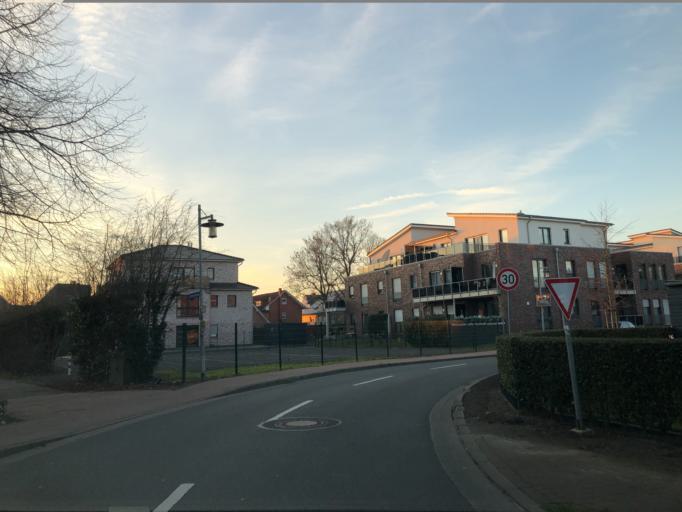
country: DE
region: Lower Saxony
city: Papenburg
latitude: 53.0859
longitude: 7.3908
